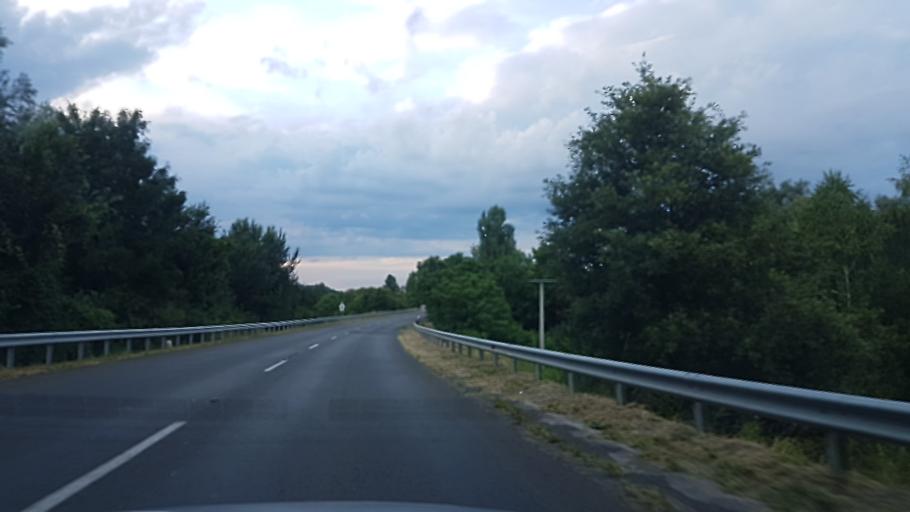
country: HU
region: Somogy
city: Kaposvar
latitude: 46.2839
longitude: 17.8192
